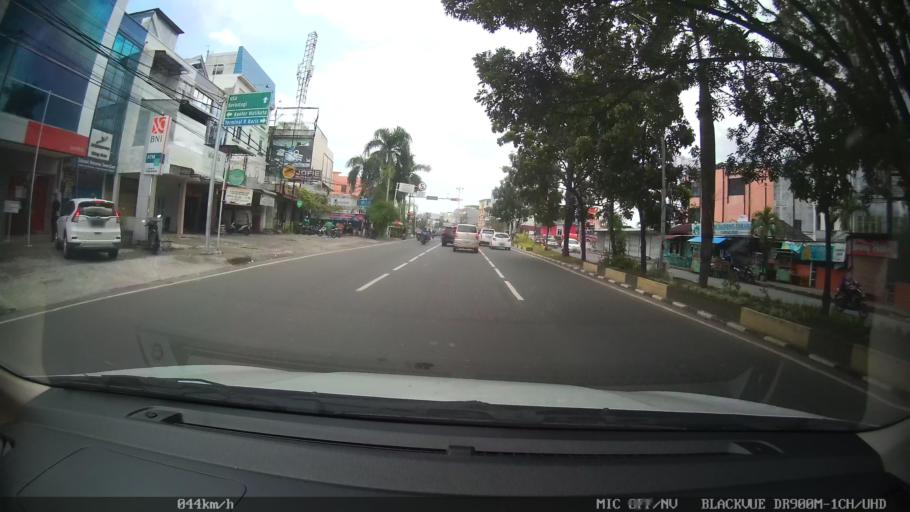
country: ID
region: North Sumatra
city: Medan
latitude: 3.6057
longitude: 98.6459
